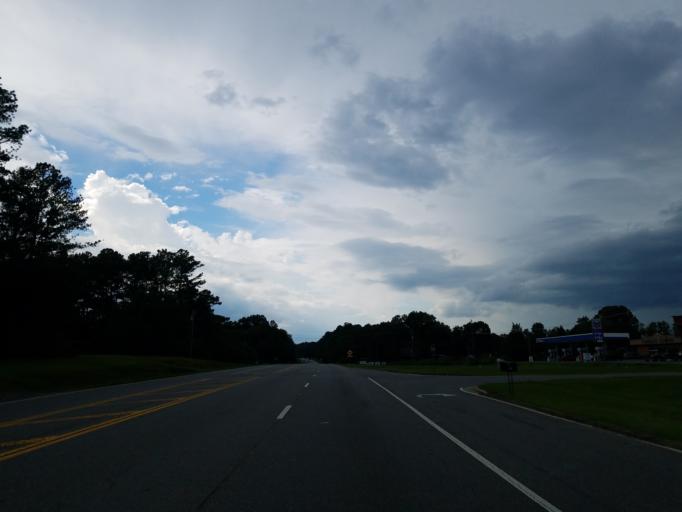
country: US
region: Georgia
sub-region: Bartow County
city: Adairsville
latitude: 34.3439
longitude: -84.9098
